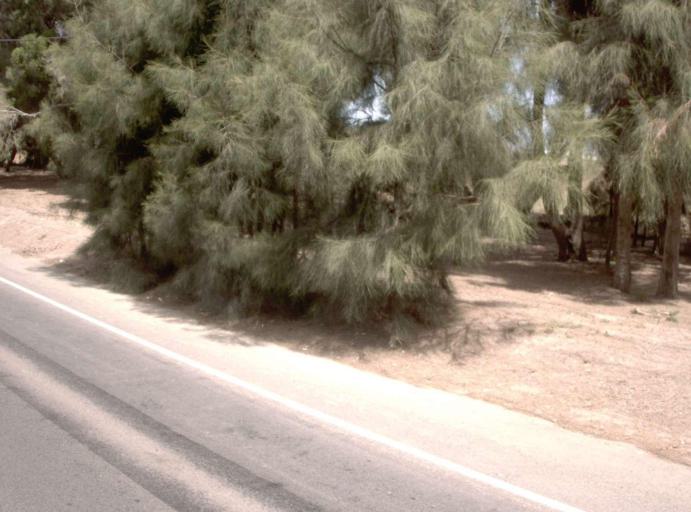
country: AU
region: Victoria
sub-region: Monash
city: Oakleigh South
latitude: -37.9430
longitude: 145.0923
